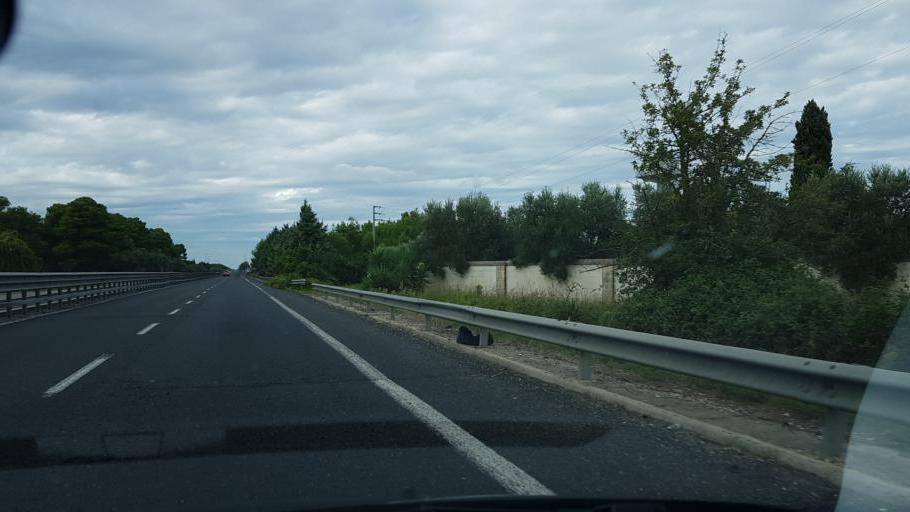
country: IT
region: Apulia
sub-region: Provincia di Lecce
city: San Donato di Lecce
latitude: 40.2841
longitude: 18.2005
